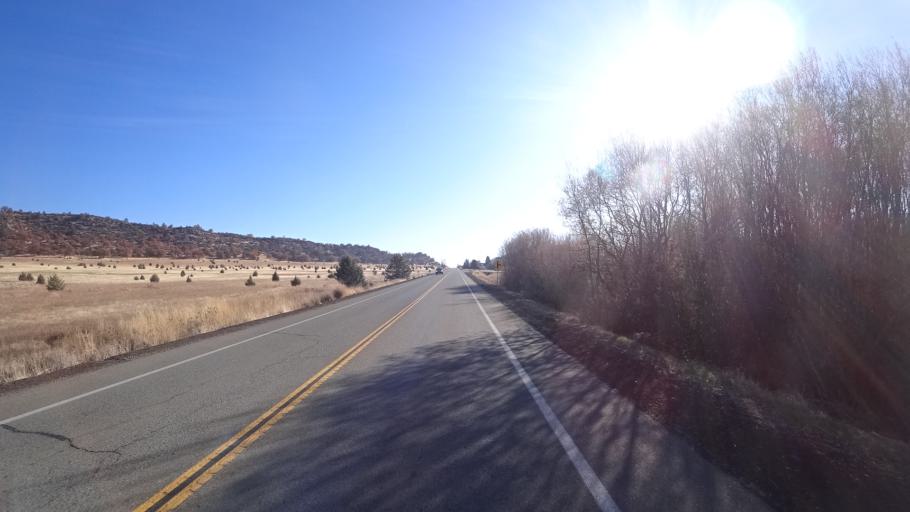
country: US
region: California
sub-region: Siskiyou County
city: Yreka
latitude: 41.7142
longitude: -122.6256
